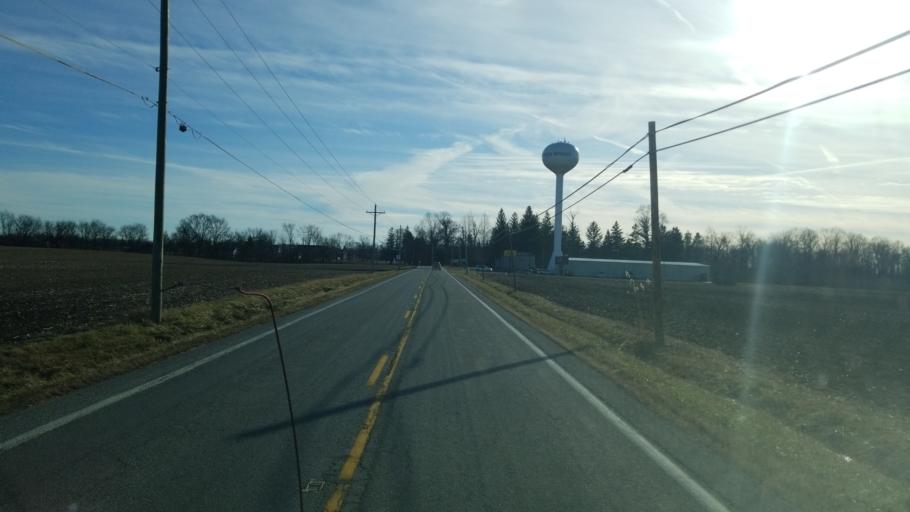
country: US
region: Ohio
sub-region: Sandusky County
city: Green Springs
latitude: 41.2683
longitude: -83.0524
